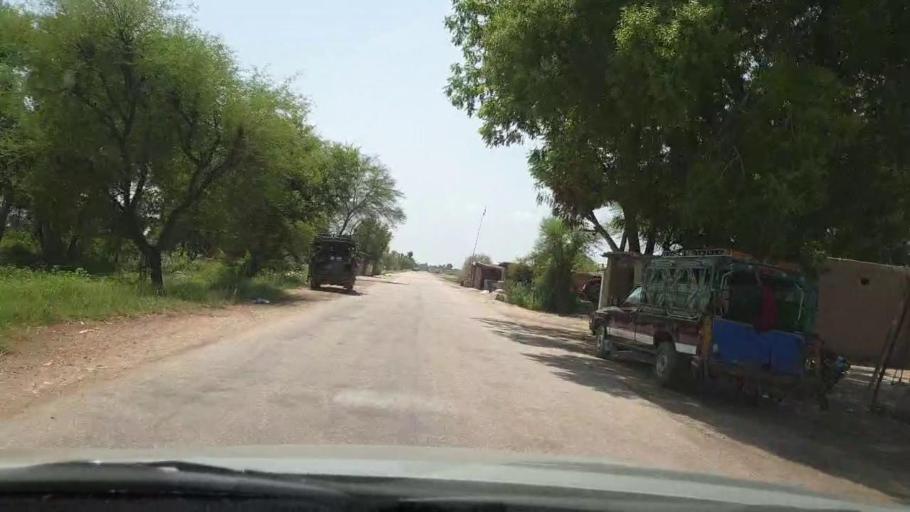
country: PK
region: Sindh
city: Pano Aqil
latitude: 27.6695
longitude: 69.0976
